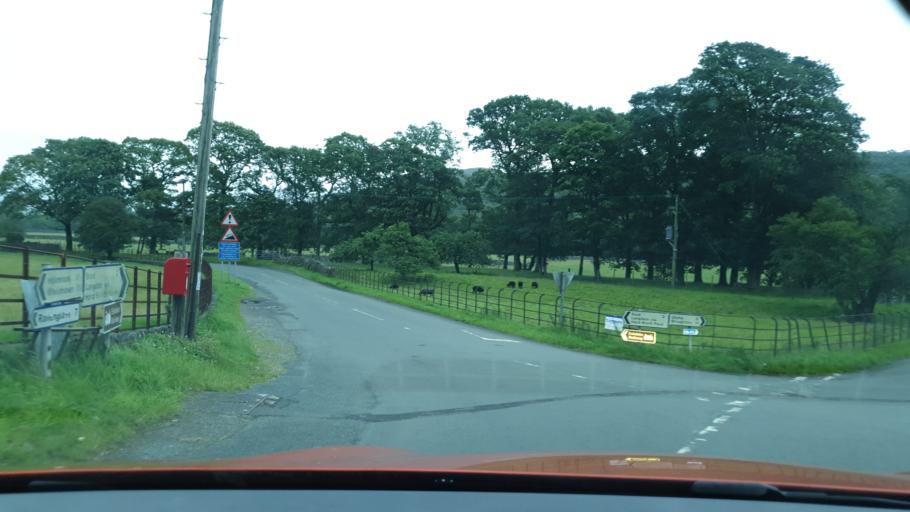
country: GB
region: England
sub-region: Cumbria
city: Seascale
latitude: 54.3868
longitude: -3.3122
